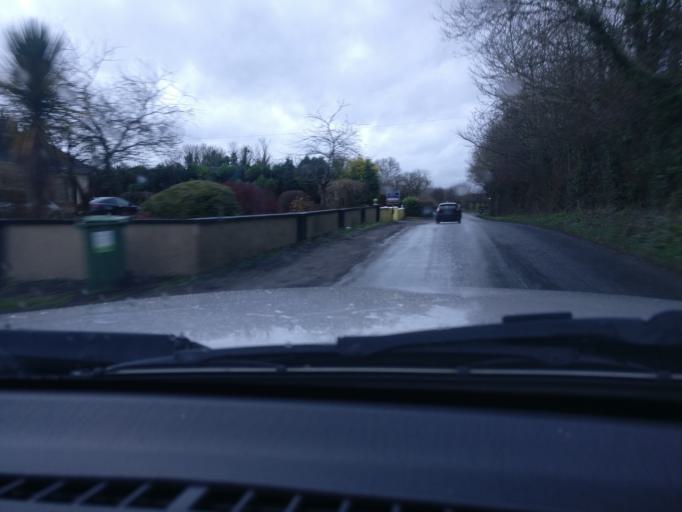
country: IE
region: Leinster
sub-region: An Mhi
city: Longwood
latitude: 53.4420
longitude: -6.9818
